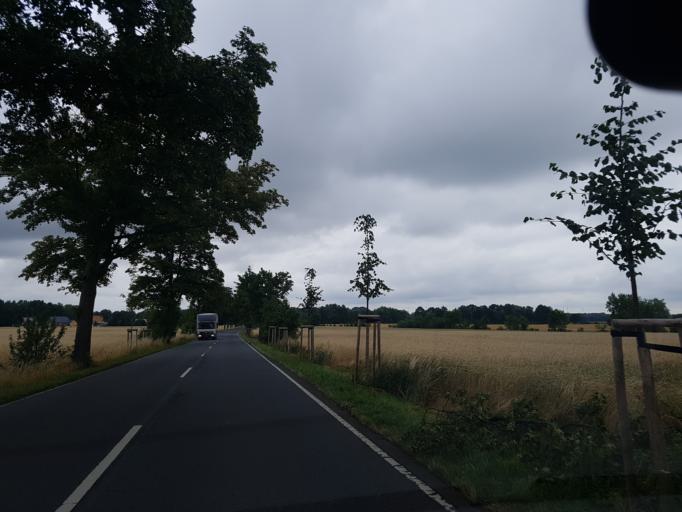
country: DE
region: Brandenburg
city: Luckau
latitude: 51.8345
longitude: 13.6876
